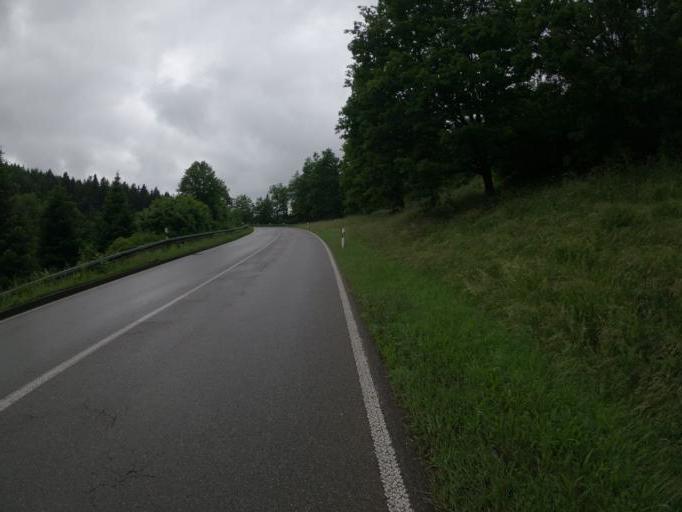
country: DE
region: Baden-Wuerttemberg
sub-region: Regierungsbezirk Stuttgart
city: Bortlingen
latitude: 48.7513
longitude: 9.6172
